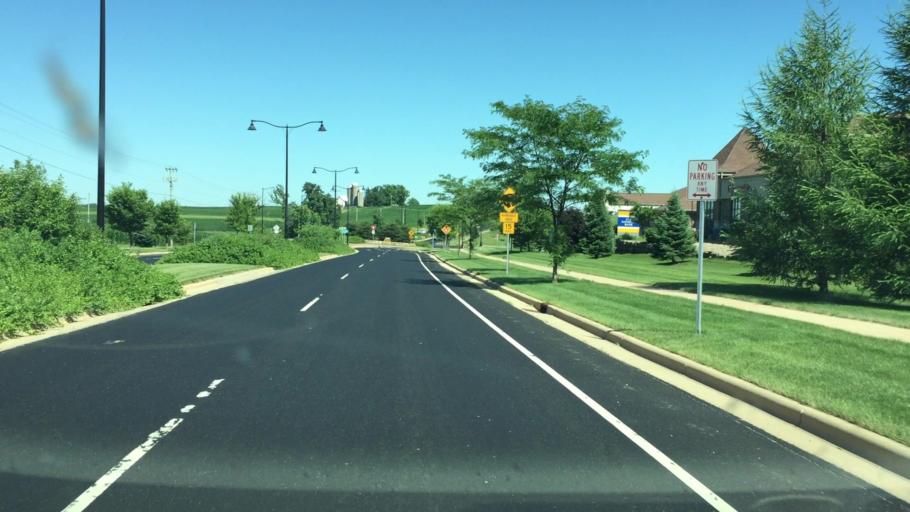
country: US
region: Wisconsin
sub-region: Dane County
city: Mount Horeb
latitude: 43.0095
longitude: -89.7127
